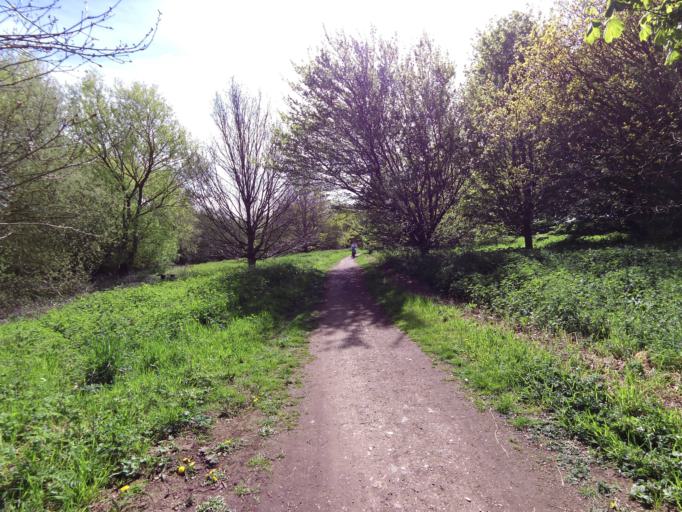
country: GB
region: England
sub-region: Essex
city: Mistley
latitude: 51.9876
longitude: 1.1156
